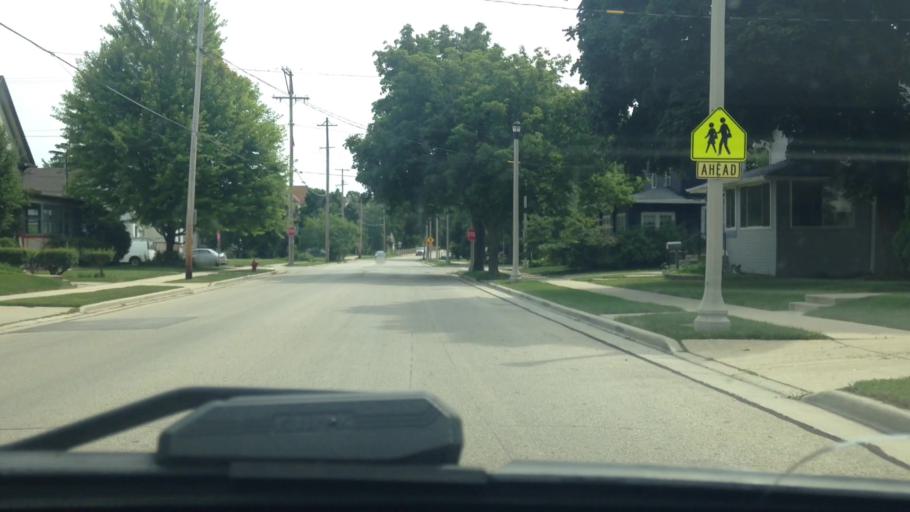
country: US
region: Wisconsin
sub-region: Waukesha County
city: Menomonee Falls
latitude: 43.1817
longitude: -88.1173
